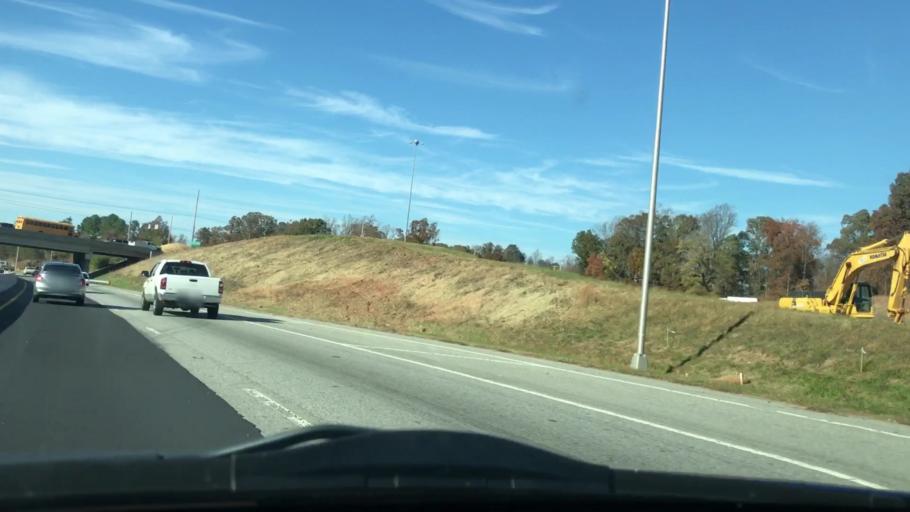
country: US
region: North Carolina
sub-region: Guilford County
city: High Point
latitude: 36.0010
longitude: -79.9907
